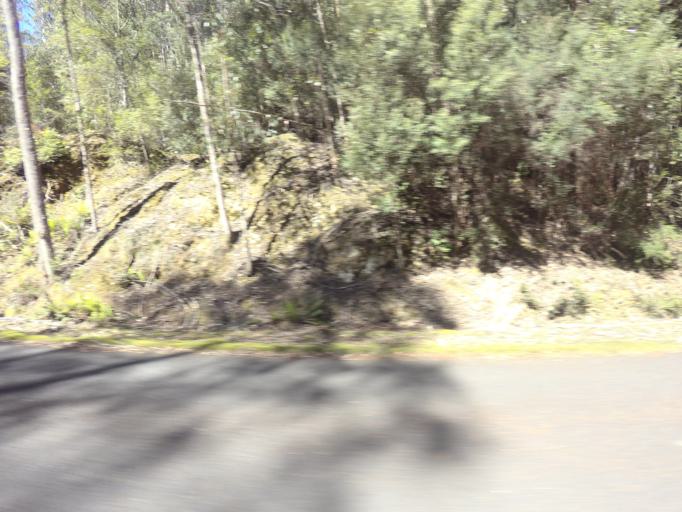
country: AU
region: Tasmania
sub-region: Huon Valley
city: Geeveston
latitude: -42.8268
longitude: 146.3239
